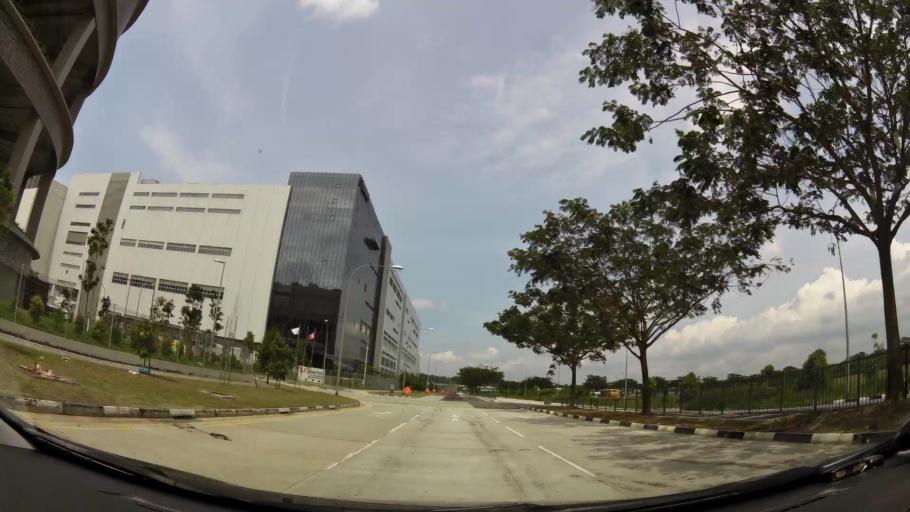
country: MY
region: Johor
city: Johor Bahru
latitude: 1.3542
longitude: 103.7100
